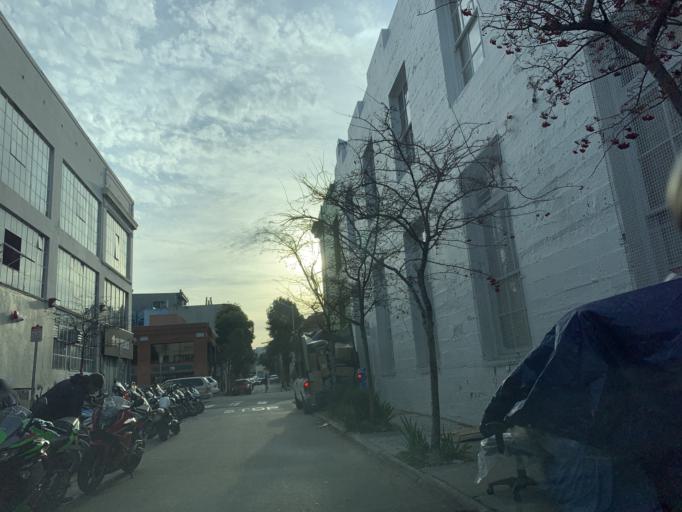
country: US
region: California
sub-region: San Francisco County
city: San Francisco
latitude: 37.7757
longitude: -122.4103
